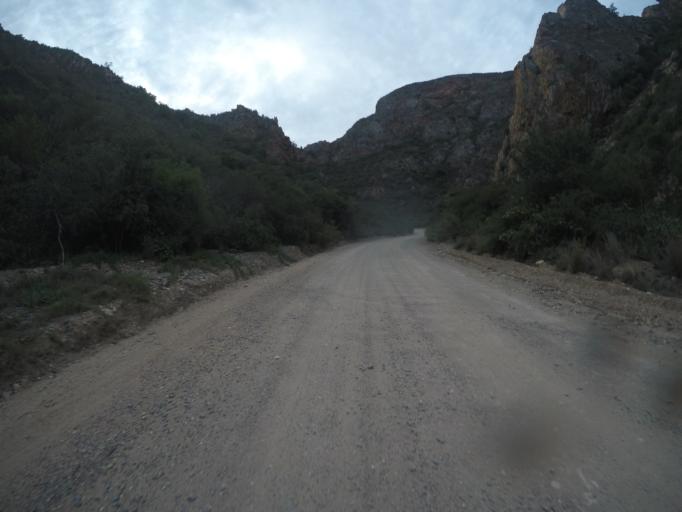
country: ZA
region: Eastern Cape
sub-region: Cacadu District Municipality
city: Willowmore
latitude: -33.5134
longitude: 23.6431
